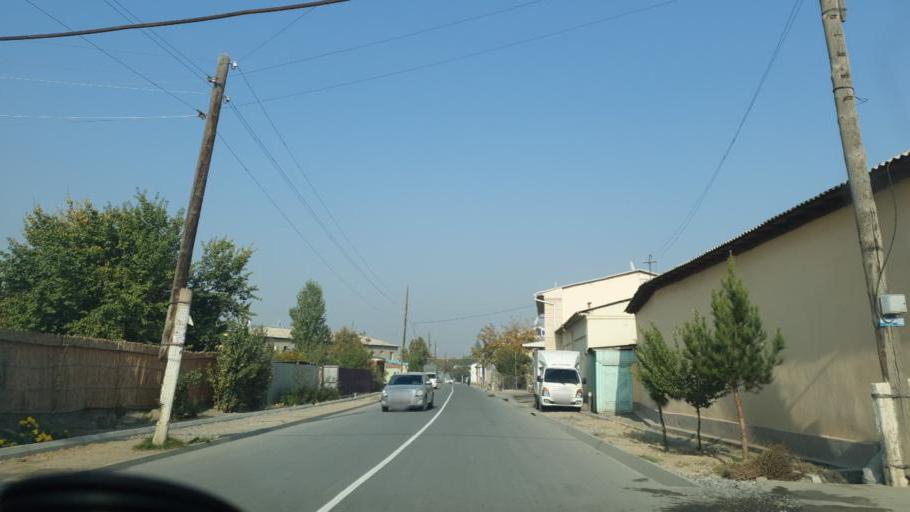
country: UZ
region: Fergana
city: Qo`qon
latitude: 40.5823
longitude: 70.9106
